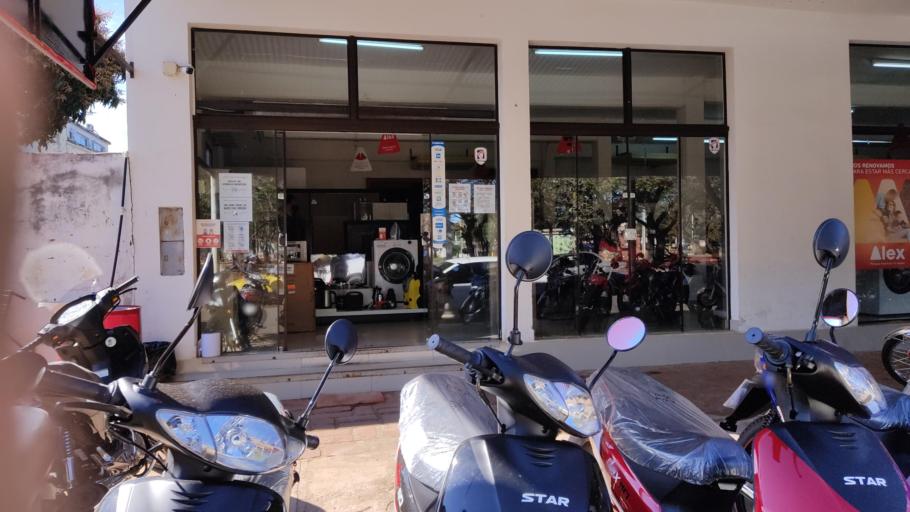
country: PY
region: Misiones
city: San Juan Bautista
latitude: -26.6699
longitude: -57.1392
